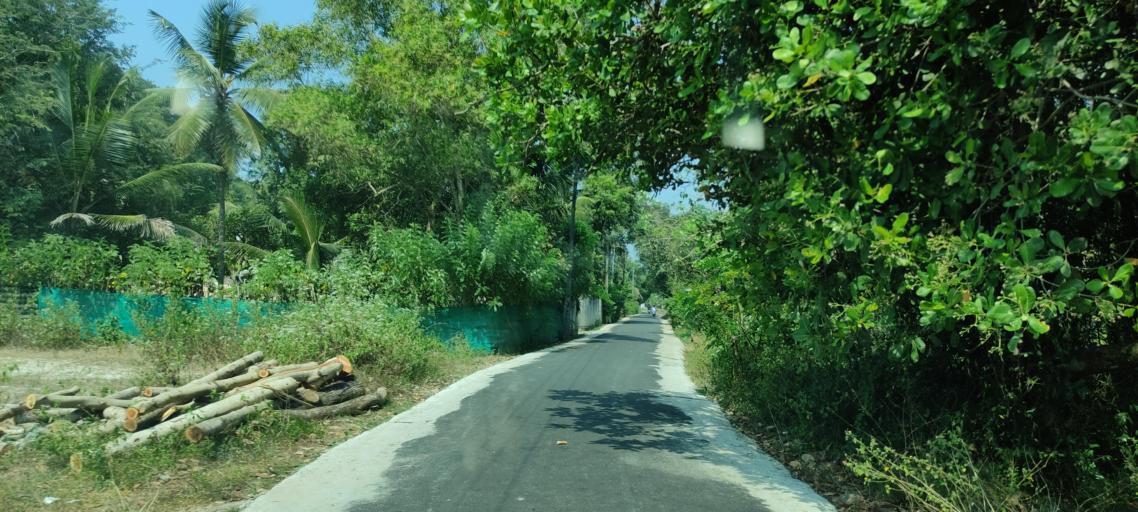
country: IN
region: Kerala
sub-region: Alappuzha
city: Alleppey
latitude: 9.5441
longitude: 76.3201
